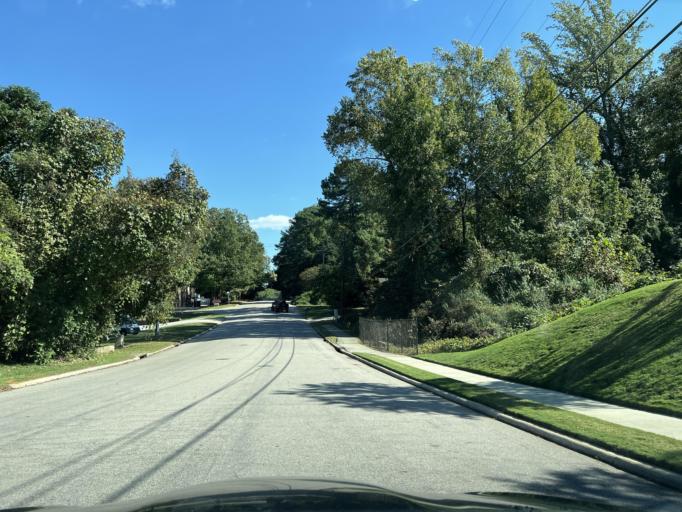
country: US
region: North Carolina
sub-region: Wake County
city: Raleigh
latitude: 35.7547
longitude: -78.6650
